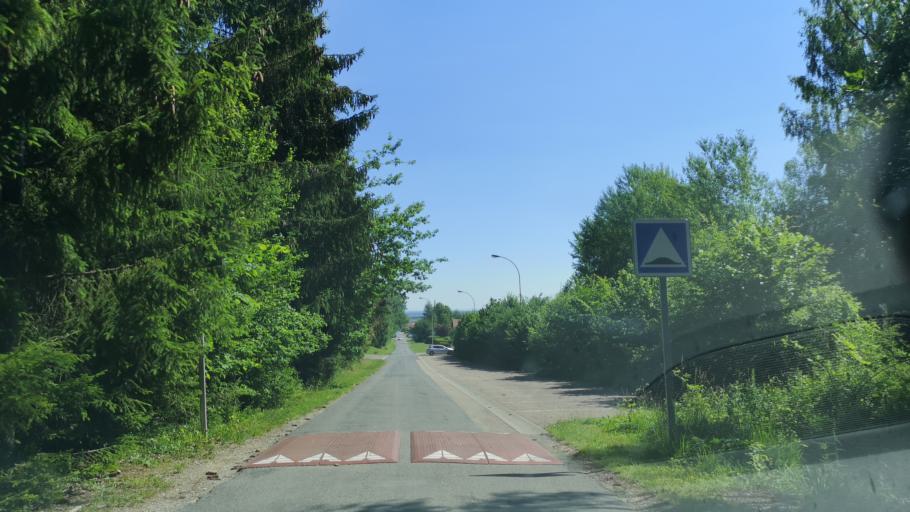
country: FR
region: Lorraine
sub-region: Departement de la Meuse
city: Vigneulles-les-Hattonchatel
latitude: 49.0336
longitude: 5.6509
